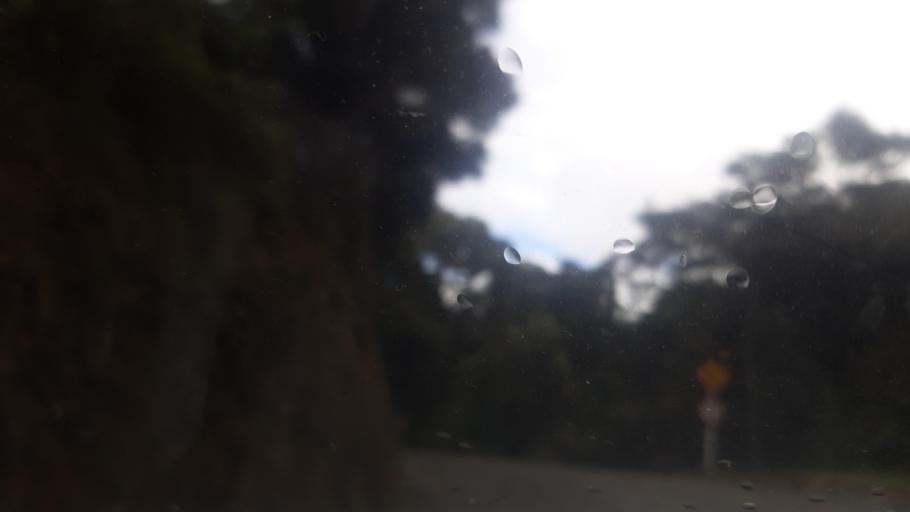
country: NZ
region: Northland
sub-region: Far North District
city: Taipa
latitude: -35.0479
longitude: 173.3925
